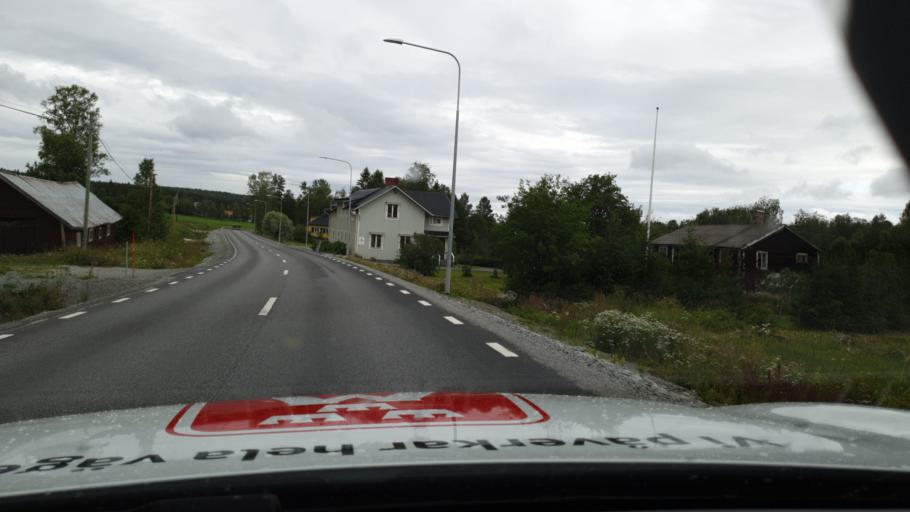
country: SE
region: Jaemtland
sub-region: Bergs Kommun
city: Hoverberg
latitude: 62.7595
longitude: 14.4264
